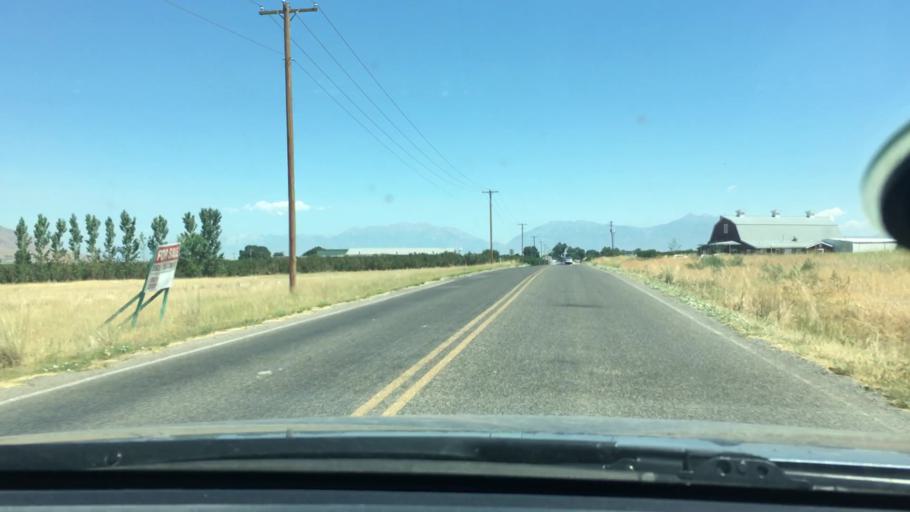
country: US
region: Utah
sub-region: Utah County
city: Santaquin
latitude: 39.9592
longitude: -111.7961
